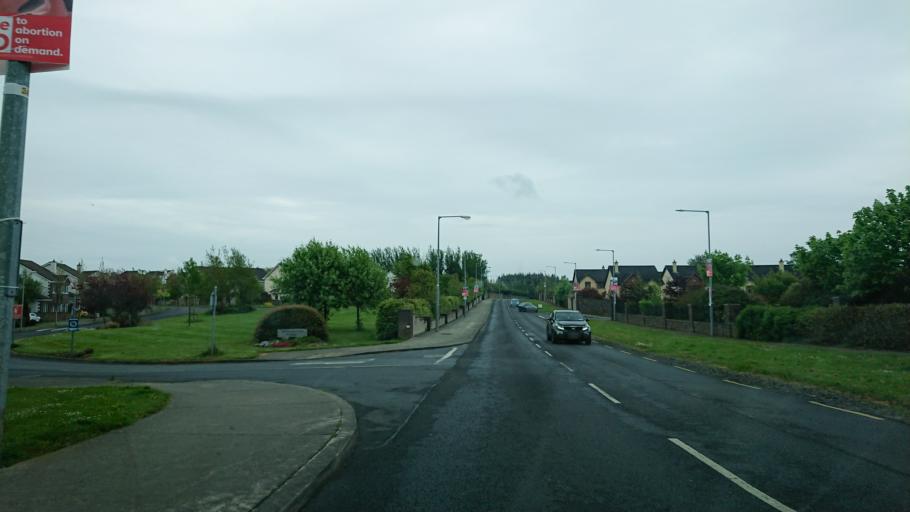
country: IE
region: Munster
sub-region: Waterford
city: Waterford
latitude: 52.2350
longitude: -7.0769
